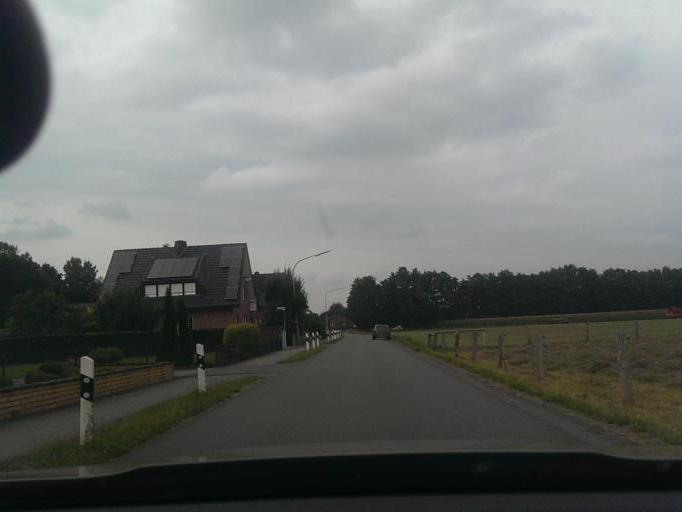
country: DE
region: North Rhine-Westphalia
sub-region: Regierungsbezirk Detmold
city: Delbruck
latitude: 51.7541
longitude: 8.5537
